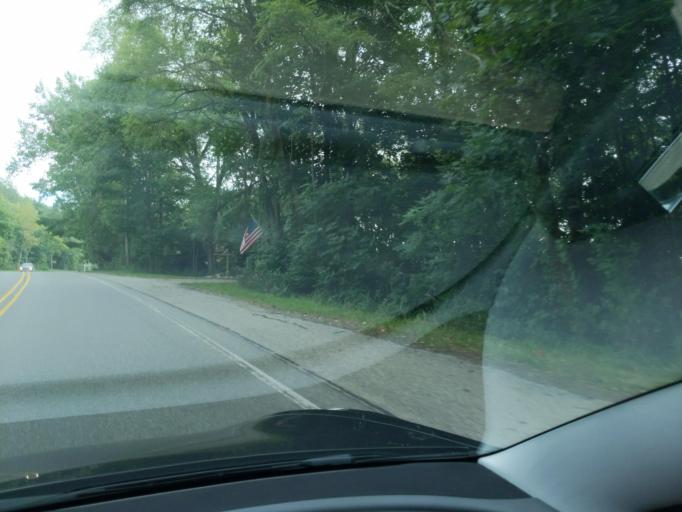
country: US
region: Michigan
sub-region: Kalkaska County
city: Rapid City
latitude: 44.8729
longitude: -85.2786
